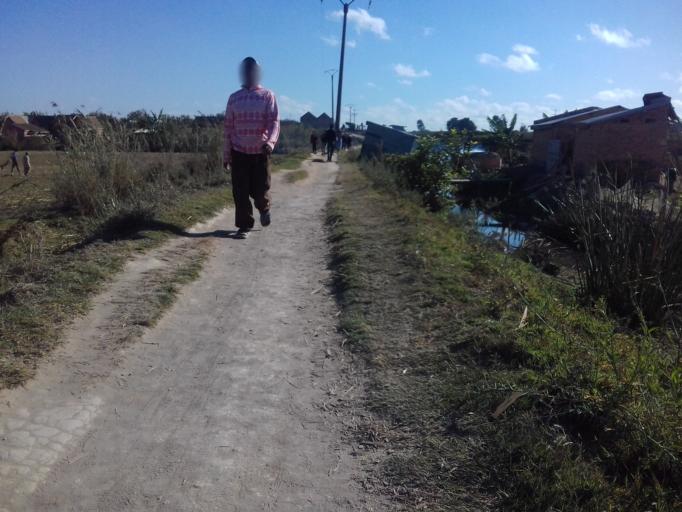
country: MG
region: Analamanga
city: Antananarivo
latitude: -18.8894
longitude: 47.4858
